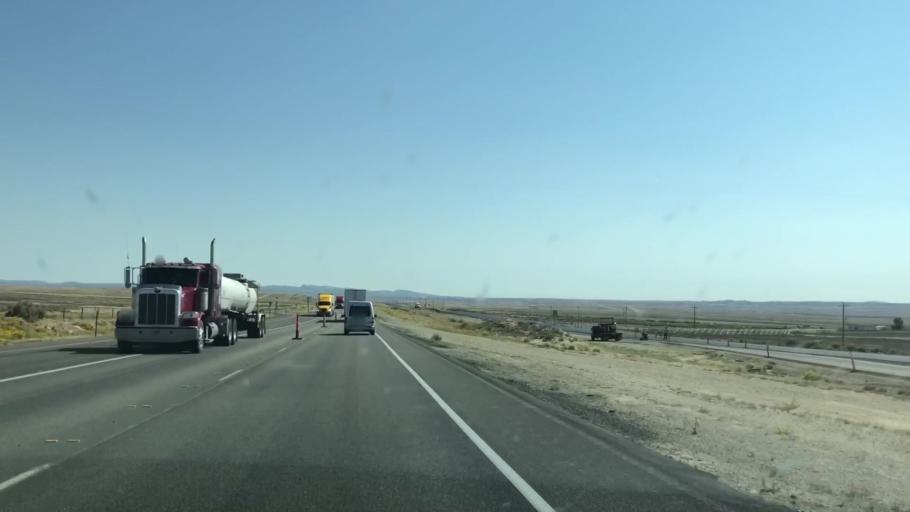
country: US
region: Wyoming
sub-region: Carbon County
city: Rawlins
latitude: 41.7507
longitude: -107.5643
